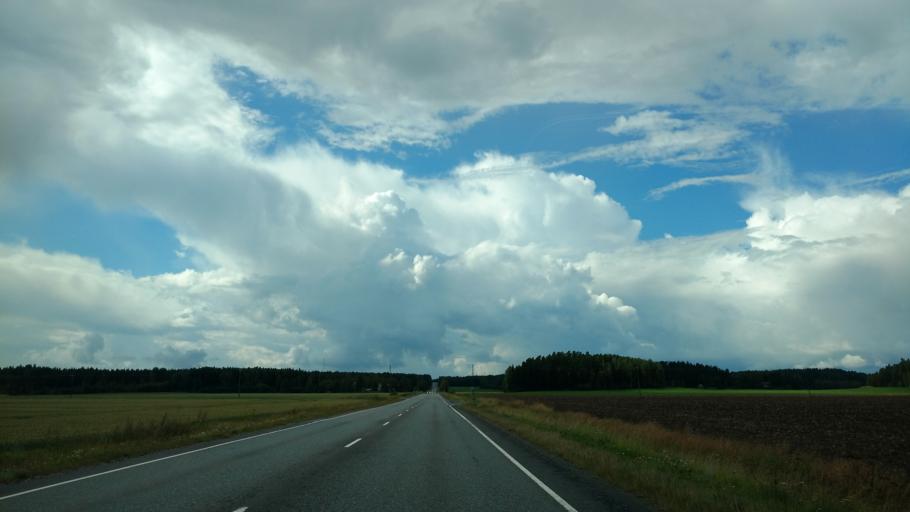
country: FI
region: Varsinais-Suomi
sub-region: Turku
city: Sauvo
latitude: 60.3932
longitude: 22.8613
